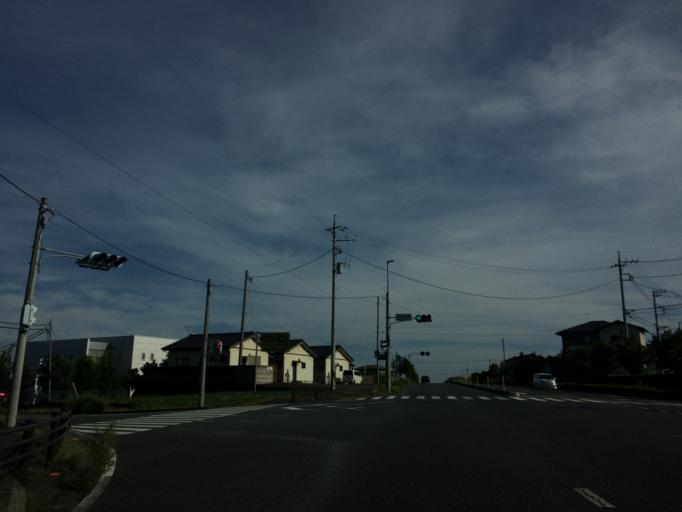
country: JP
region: Gunma
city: Shibukawa
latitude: 36.4898
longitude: 138.9966
